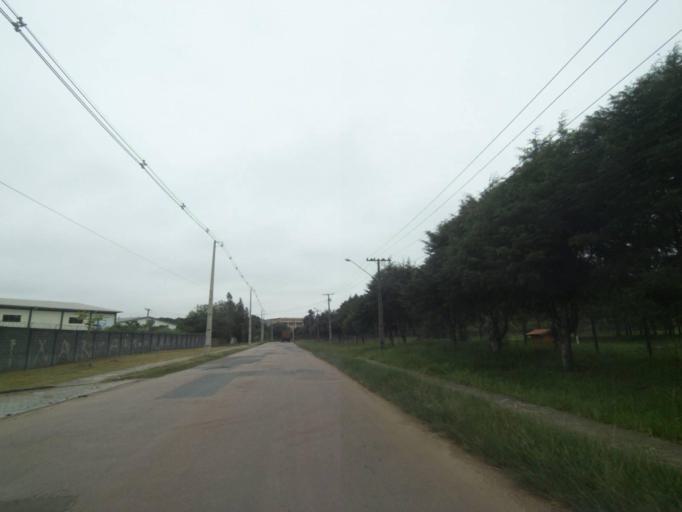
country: BR
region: Parana
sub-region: Araucaria
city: Araucaria
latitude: -25.5438
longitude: -49.3251
